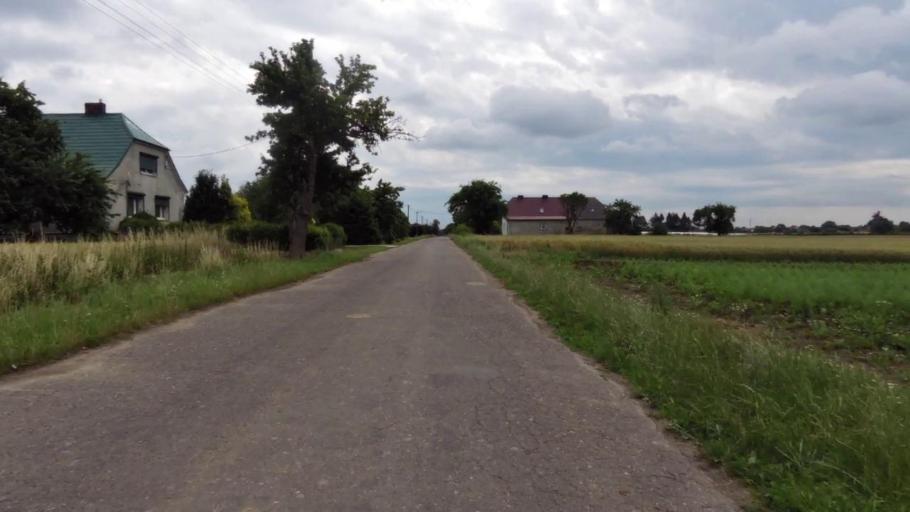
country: PL
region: West Pomeranian Voivodeship
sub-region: Powiat pyrzycki
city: Lipiany
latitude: 52.9659
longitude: 14.9495
